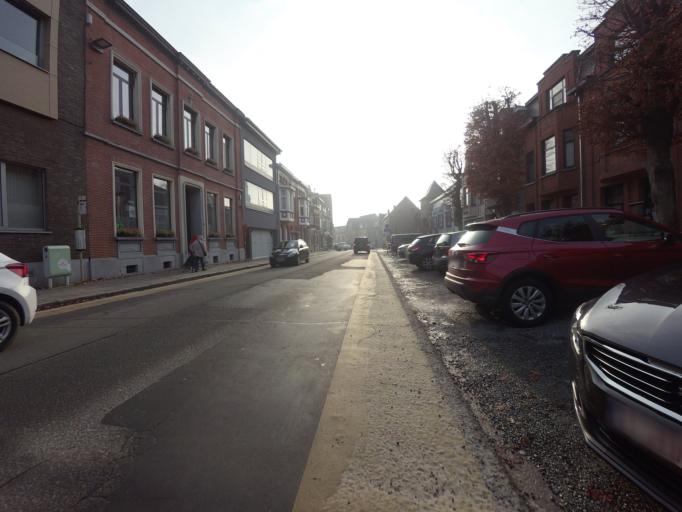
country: BE
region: Flanders
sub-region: Provincie Oost-Vlaanderen
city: Ninove
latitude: 50.8401
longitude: 4.0221
